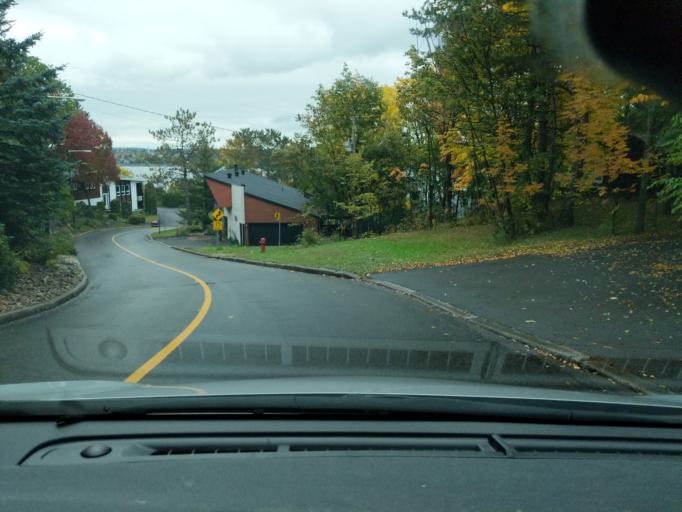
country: CA
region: Quebec
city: Quebec
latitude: 46.7637
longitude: -71.2676
